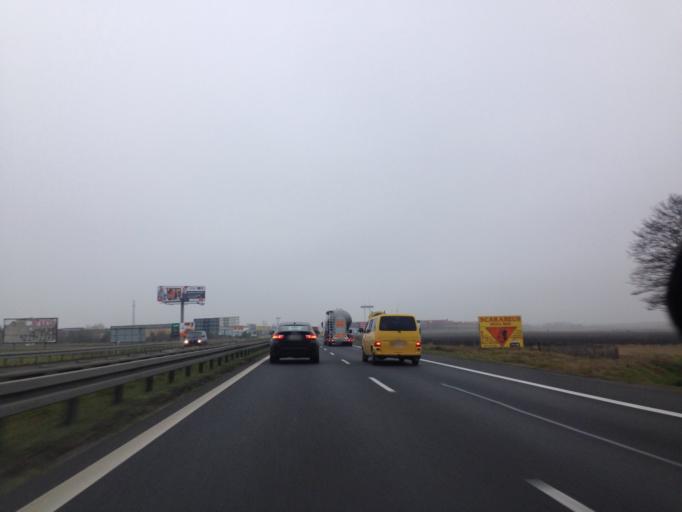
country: PL
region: Lodz Voivodeship
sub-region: Powiat lodzki wschodni
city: Rzgow
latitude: 51.6560
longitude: 19.4801
